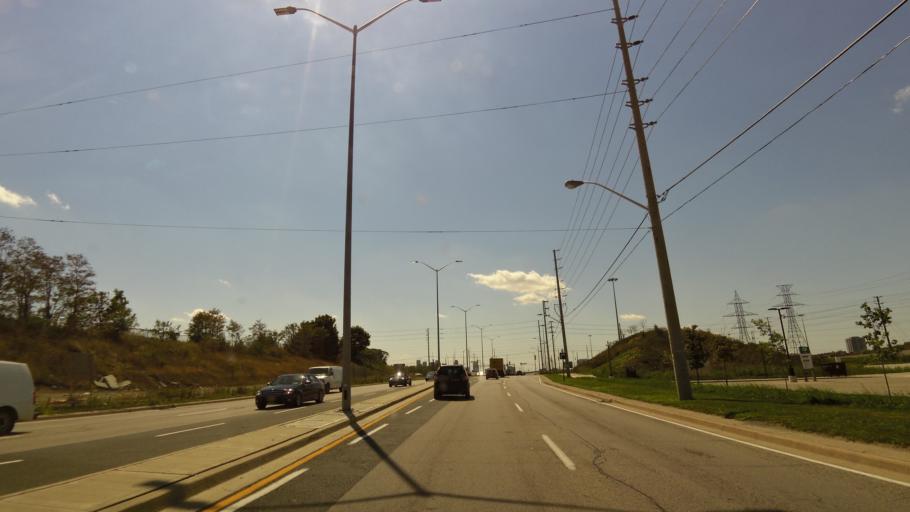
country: CA
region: Ontario
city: Mississauga
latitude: 43.6172
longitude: -79.6272
